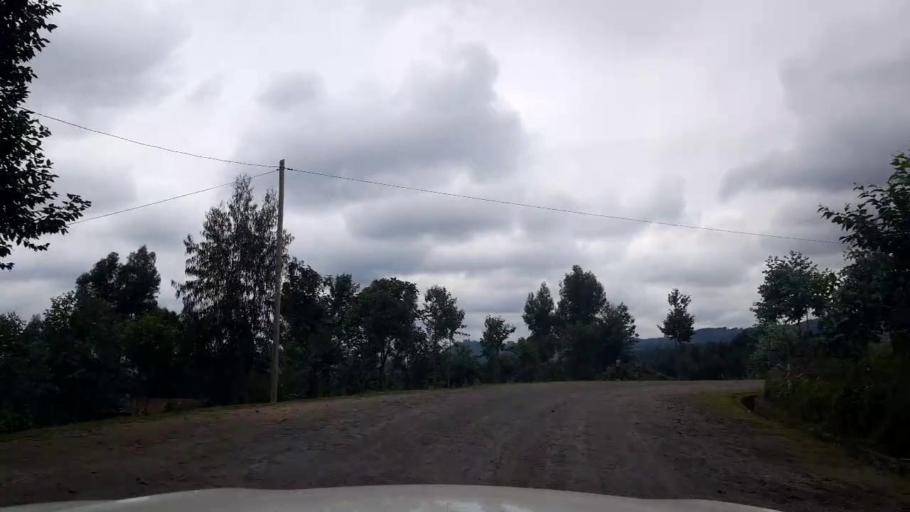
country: RW
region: Northern Province
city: Musanze
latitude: -1.5418
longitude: 29.5339
